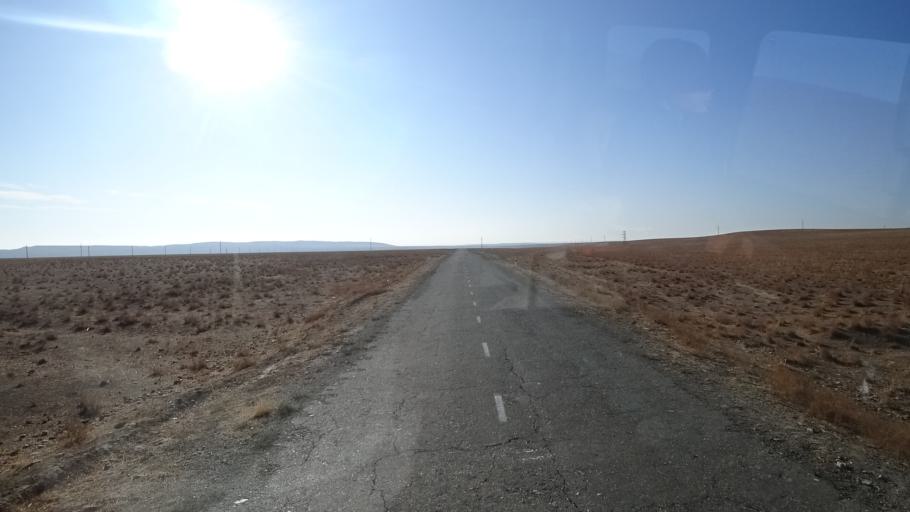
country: UZ
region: Navoiy
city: Karmana Shahri
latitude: 40.2697
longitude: 65.5251
